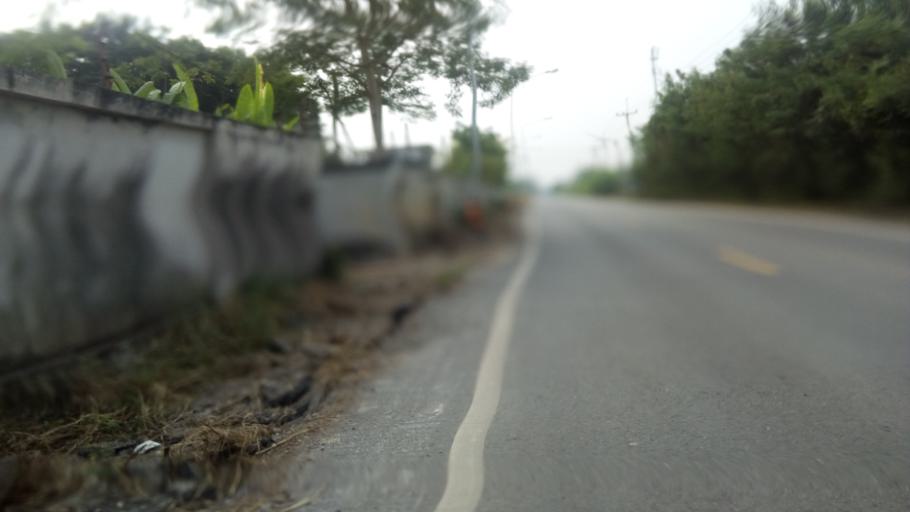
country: TH
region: Pathum Thani
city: Ban Rangsit
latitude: 14.0437
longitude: 100.8247
